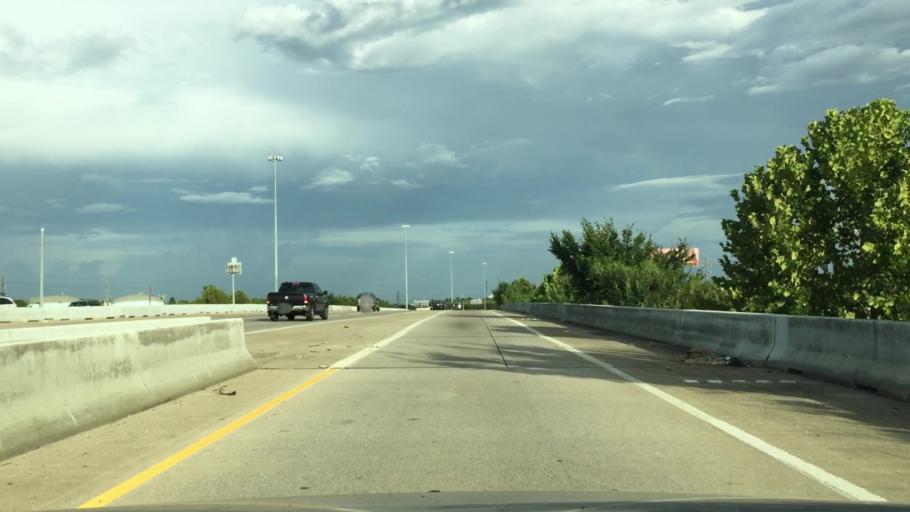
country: US
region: Texas
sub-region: Harris County
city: Hudson
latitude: 29.9536
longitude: -95.5389
